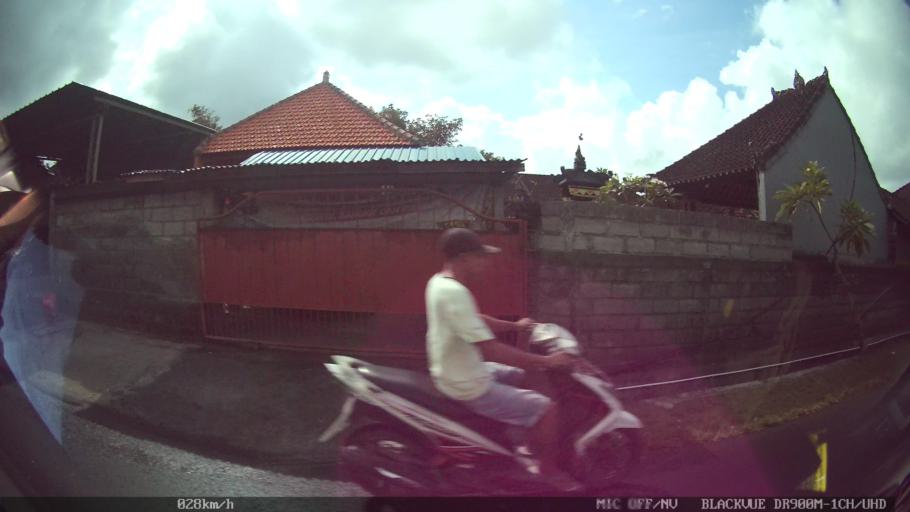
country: ID
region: Bali
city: Banjar Batur
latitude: -8.6046
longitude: 115.2061
